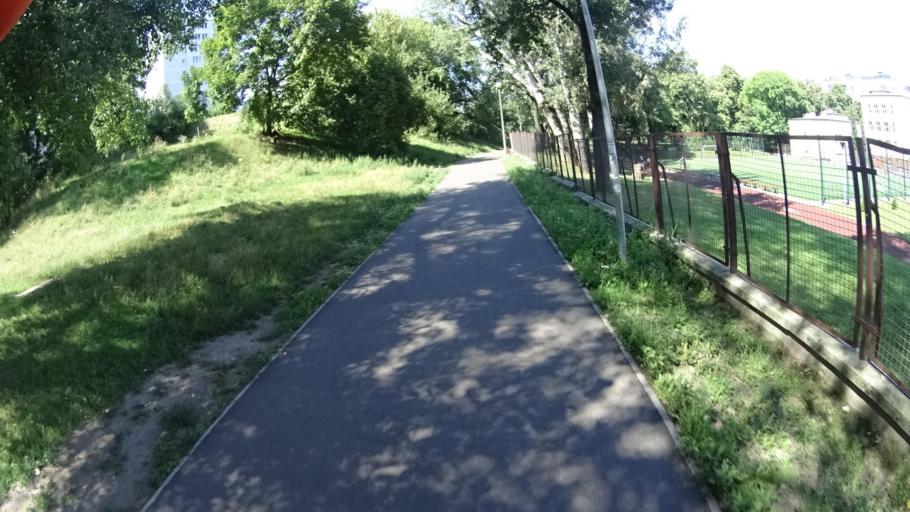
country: PL
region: Masovian Voivodeship
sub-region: Warszawa
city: Mokotow
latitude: 52.2048
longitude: 21.0271
